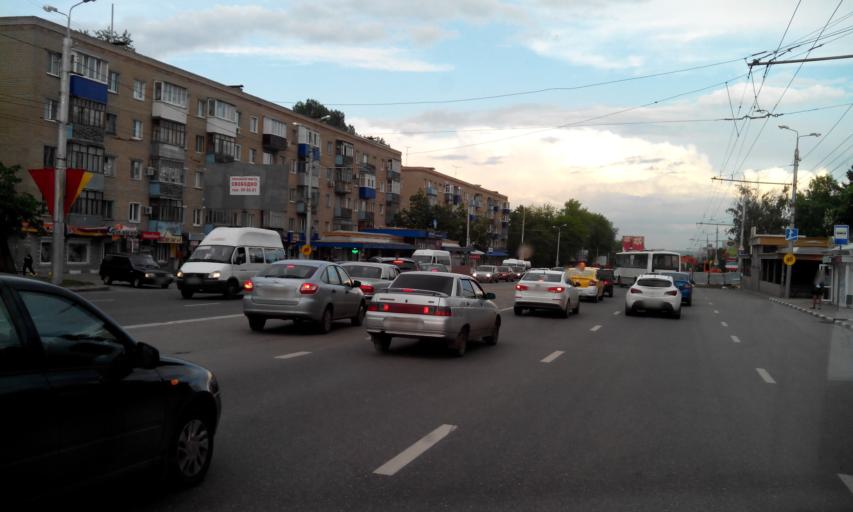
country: RU
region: Penza
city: Penza
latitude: 53.2172
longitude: 44.9797
